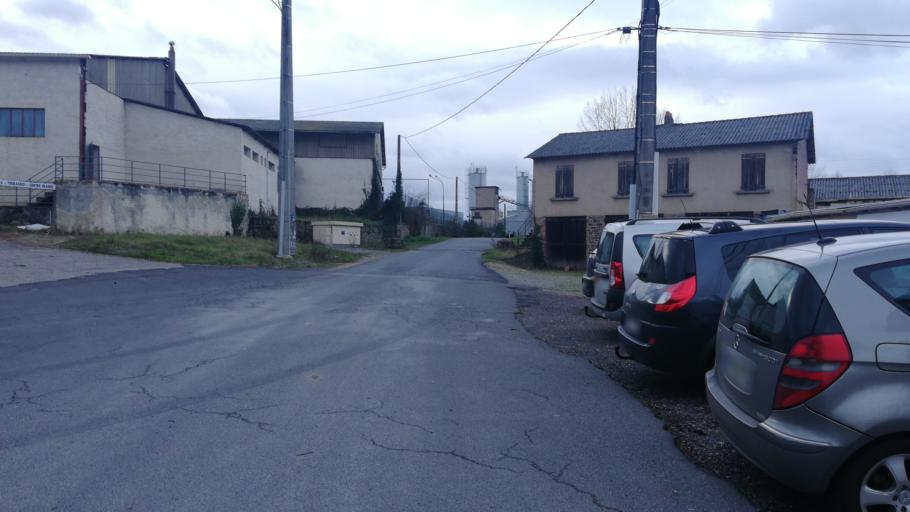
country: FR
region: Auvergne
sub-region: Departement du Puy-de-Dome
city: Lezoux
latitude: 45.7730
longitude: 3.3973
